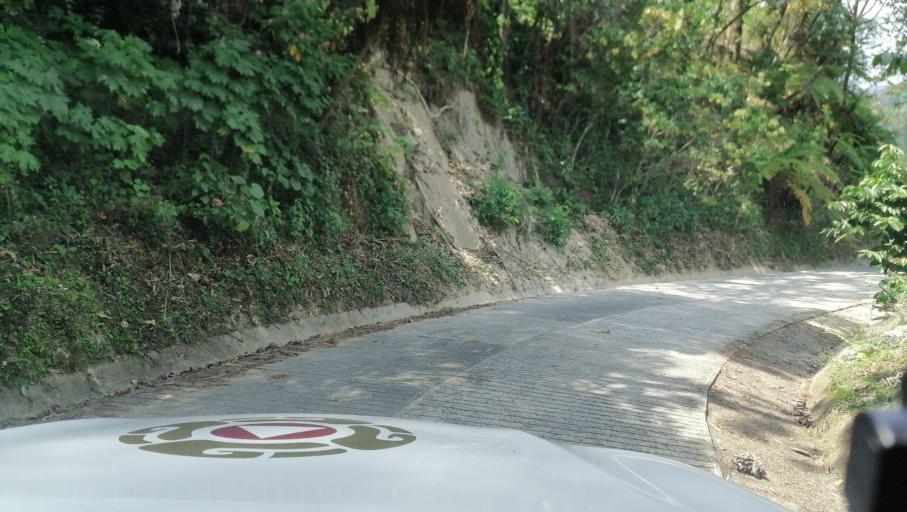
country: MX
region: Chiapas
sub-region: Tapachula
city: Canton Villaflor
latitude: 15.1348
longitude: -92.2909
